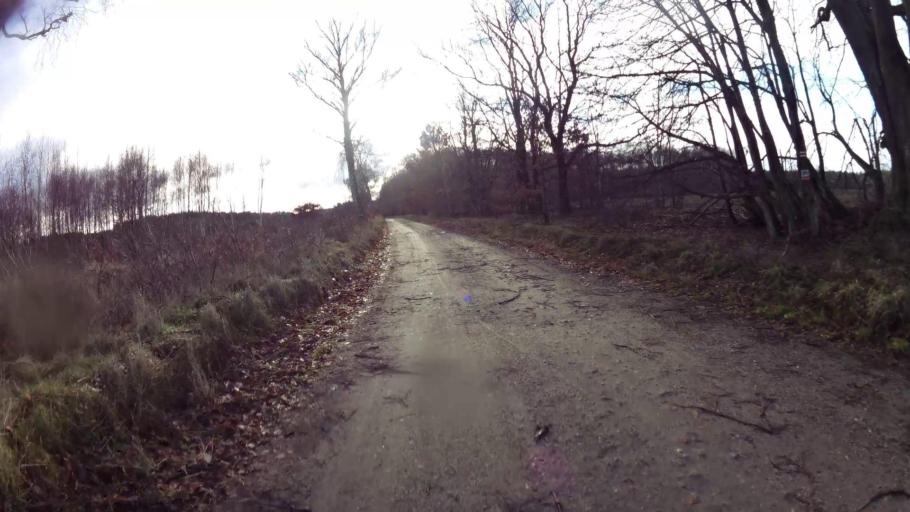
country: PL
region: West Pomeranian Voivodeship
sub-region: Powiat koszalinski
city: Sianow
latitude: 54.1225
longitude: 16.2987
